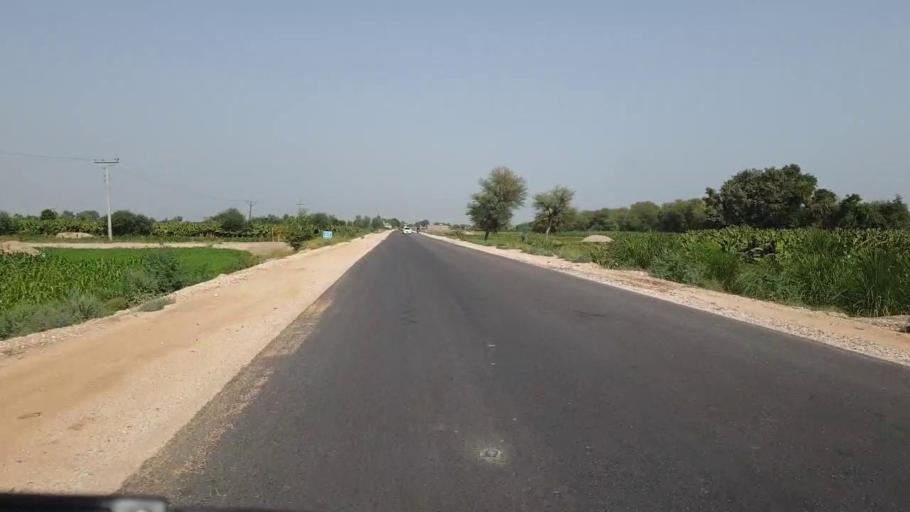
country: PK
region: Sindh
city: Sakrand
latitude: 26.2517
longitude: 68.2057
